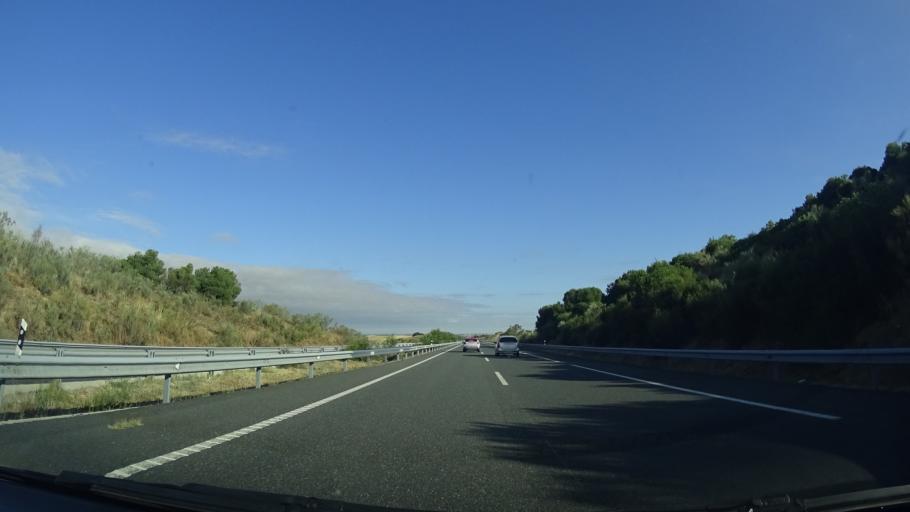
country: ES
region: Castille and Leon
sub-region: Provincia de Segovia
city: Labajos
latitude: 40.8441
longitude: -4.5391
